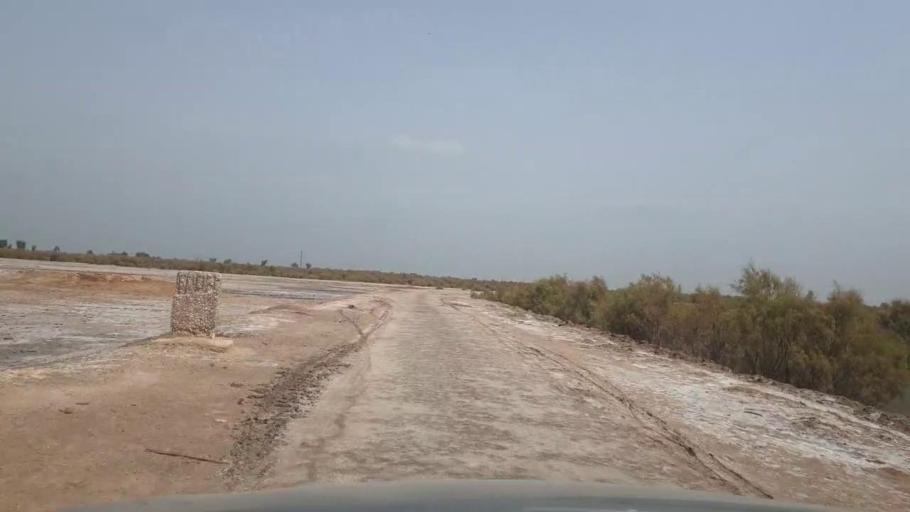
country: PK
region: Sindh
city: Garhi Yasin
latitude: 27.9519
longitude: 68.3650
